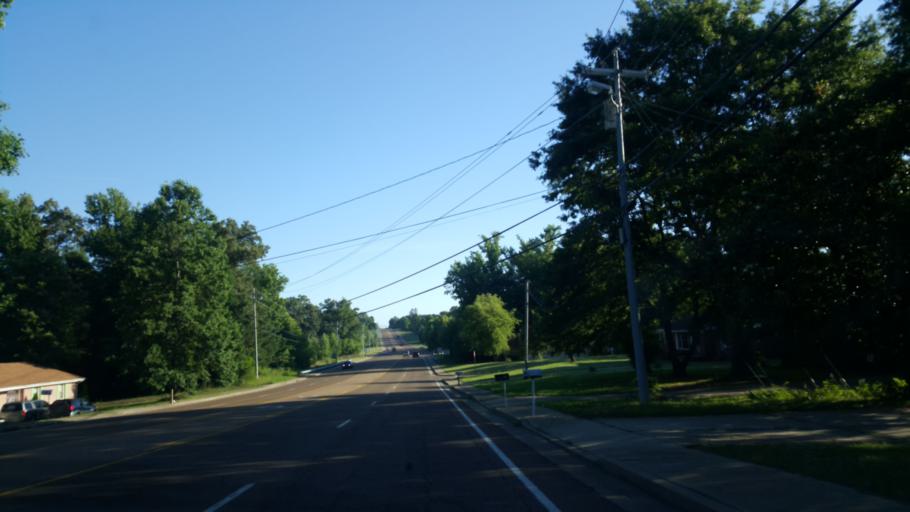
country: US
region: Tennessee
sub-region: Henderson County
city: Lexington
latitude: 35.6663
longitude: -88.3842
